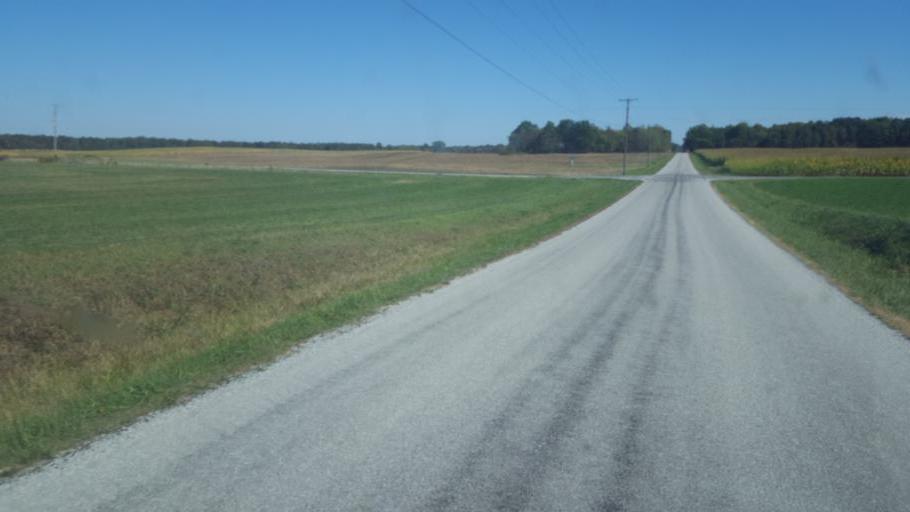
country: US
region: Ohio
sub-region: Huron County
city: Greenwich
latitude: 40.9929
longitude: -82.4339
